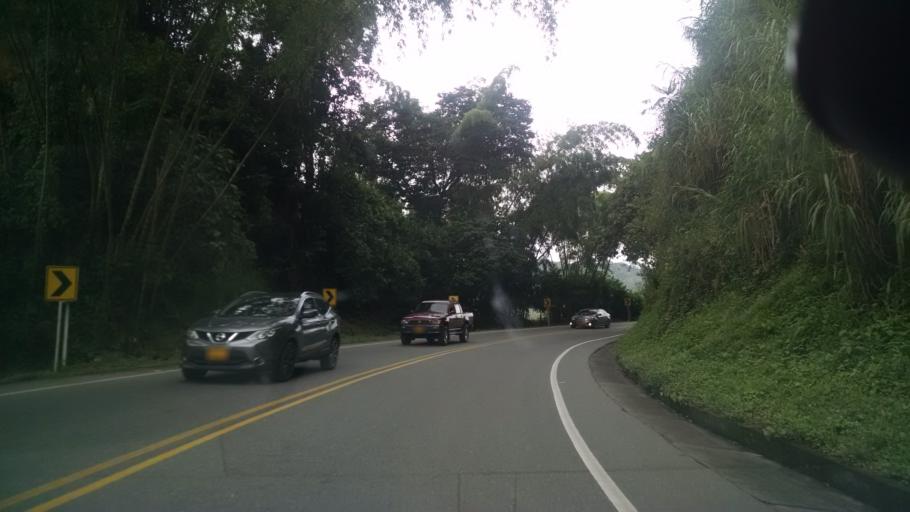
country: CO
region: Caldas
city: Palestina
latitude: 5.0683
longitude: -75.6335
